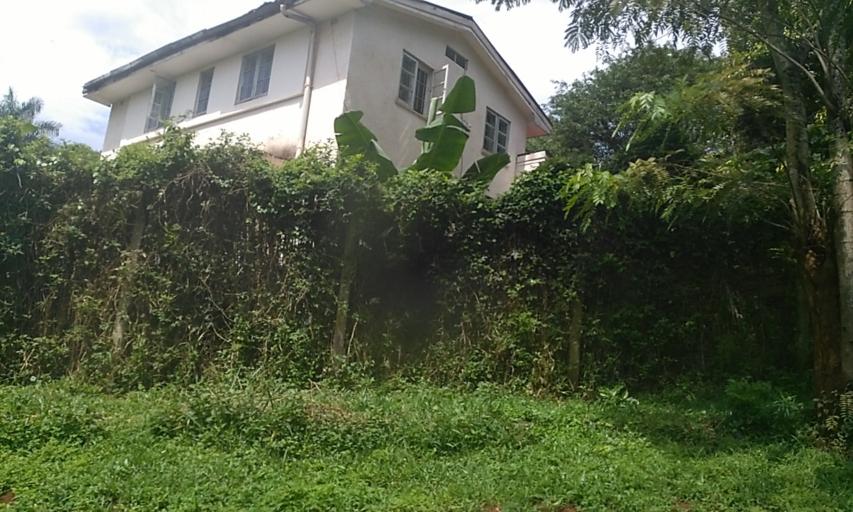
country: UG
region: Central Region
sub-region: Kampala District
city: Kampala
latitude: 0.3307
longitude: 32.5972
